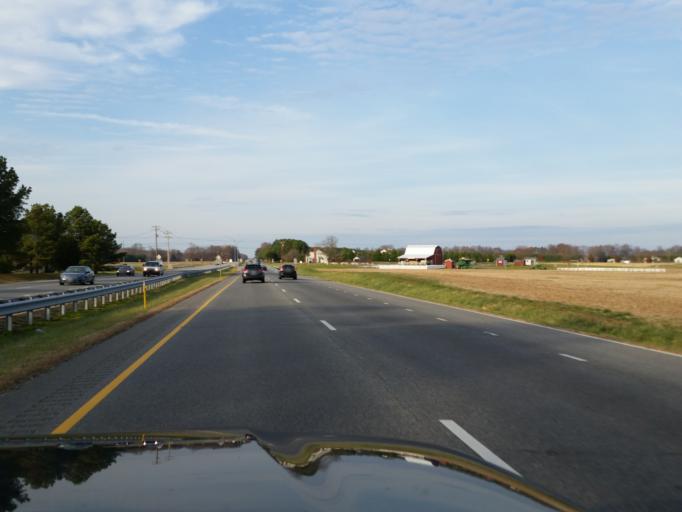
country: US
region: Maryland
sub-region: Talbot County
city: Easton
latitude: 38.8692
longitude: -76.0611
